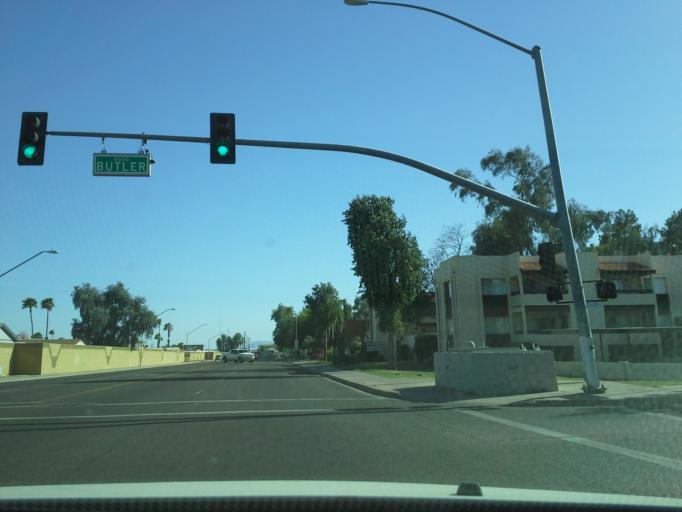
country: US
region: Arizona
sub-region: Maricopa County
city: Glendale
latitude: 33.5600
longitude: -112.2030
